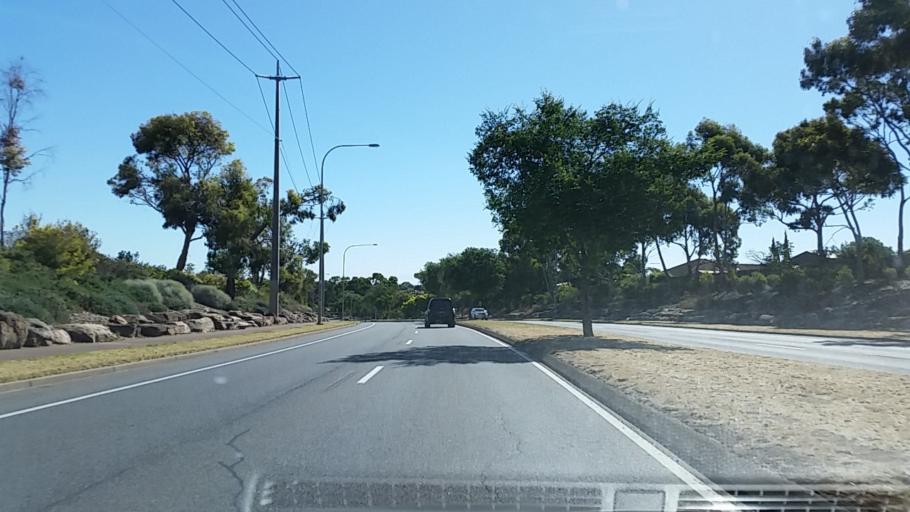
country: AU
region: South Australia
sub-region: Tea Tree Gully
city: Modbury
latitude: -34.8069
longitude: 138.6794
